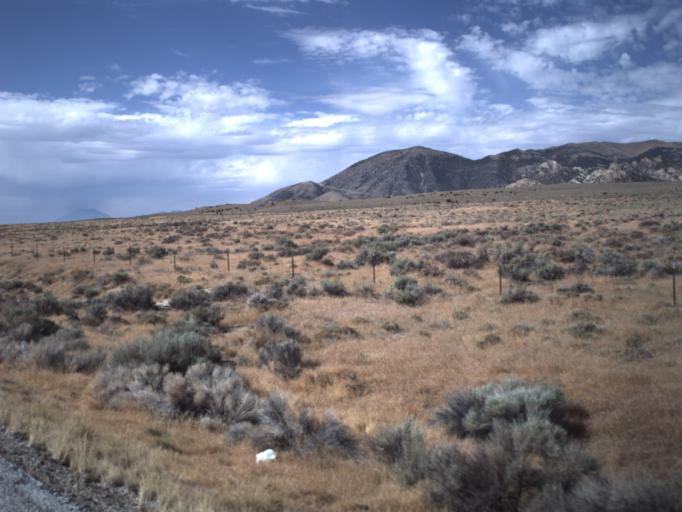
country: US
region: Utah
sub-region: Tooele County
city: Wendover
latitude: 41.5190
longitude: -113.5980
